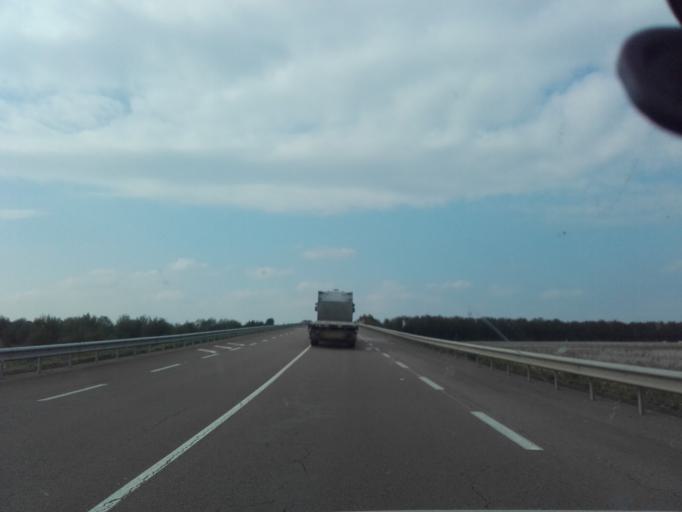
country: FR
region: Bourgogne
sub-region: Departement de Saone-et-Loire
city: Champforgeuil
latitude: 46.8086
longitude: 4.8307
